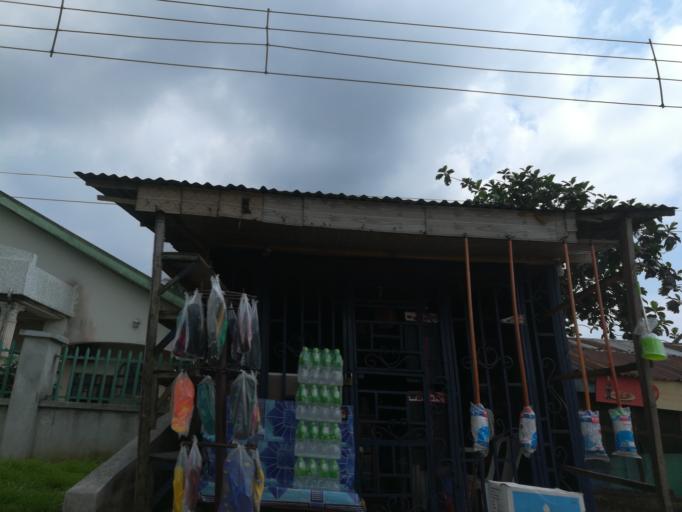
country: NG
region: Rivers
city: Okrika
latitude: 4.7274
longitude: 7.1503
